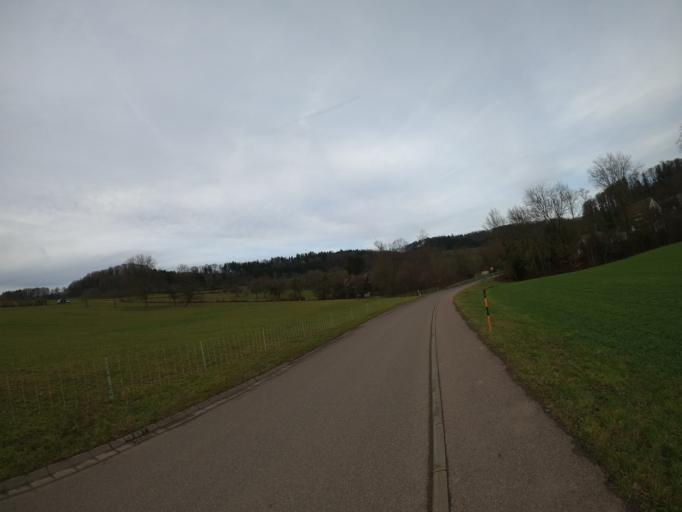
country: DE
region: Baden-Wuerttemberg
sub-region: Regierungsbezirk Stuttgart
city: Ottenbach
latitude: 48.7435
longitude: 9.7528
